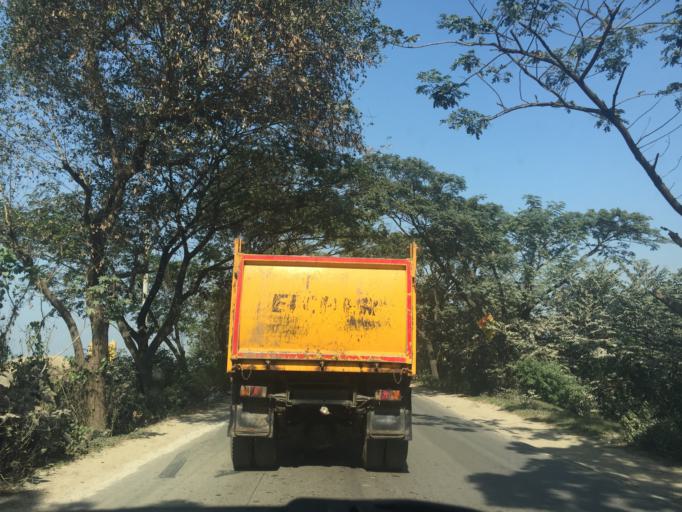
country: BD
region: Dhaka
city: Tungi
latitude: 23.8328
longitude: 90.3403
